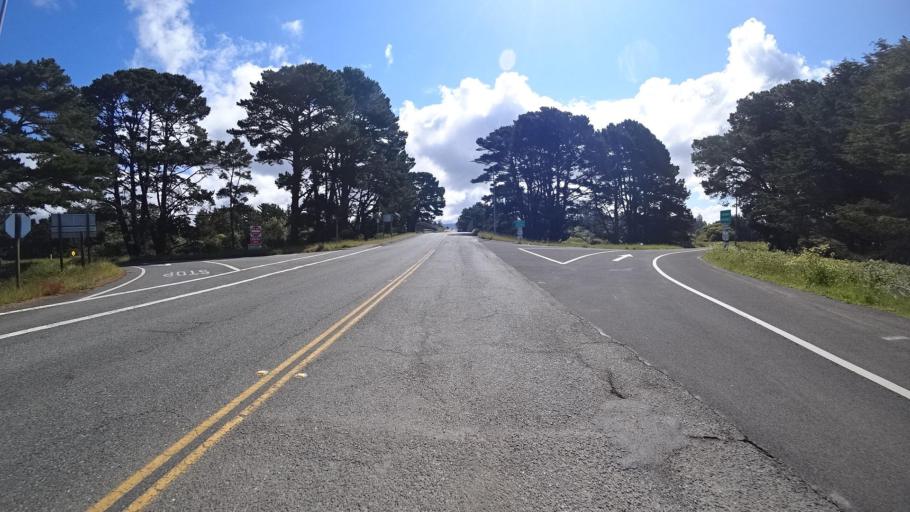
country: US
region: California
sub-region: Humboldt County
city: McKinleyville
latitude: 40.9343
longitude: -124.1163
